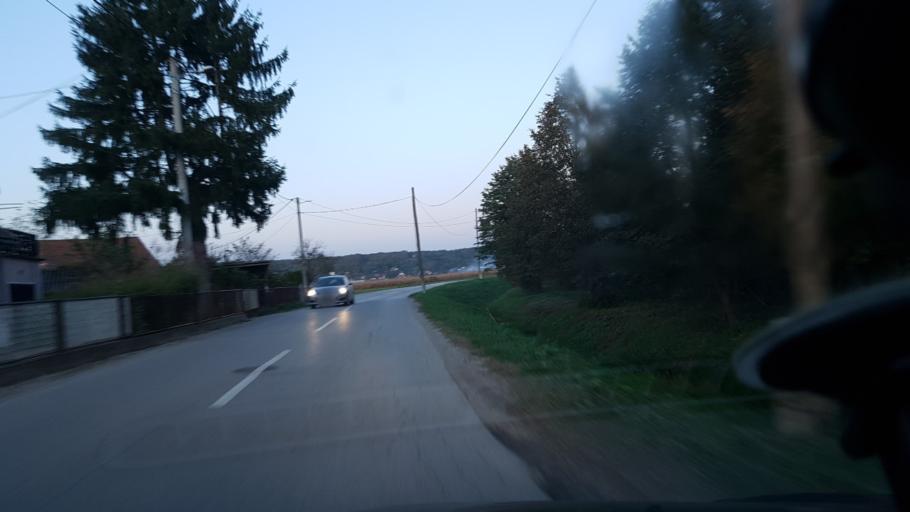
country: HR
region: Zagrebacka
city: Bregana
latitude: 45.8691
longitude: 15.7169
